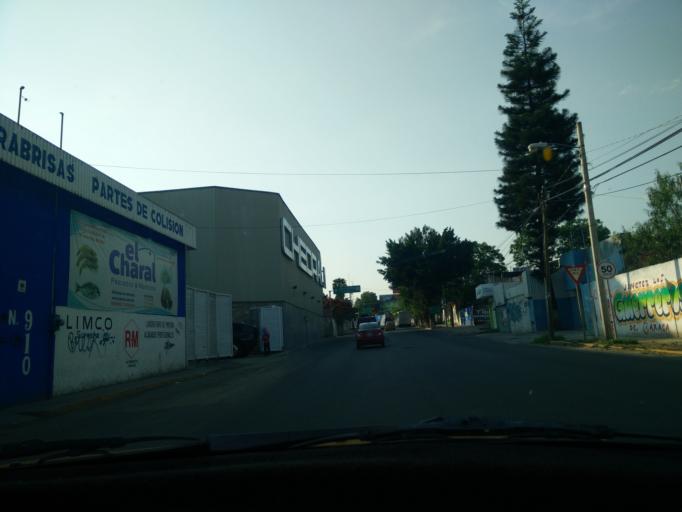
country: MX
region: Oaxaca
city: Oaxaca de Juarez
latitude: 17.0786
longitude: -96.7409
